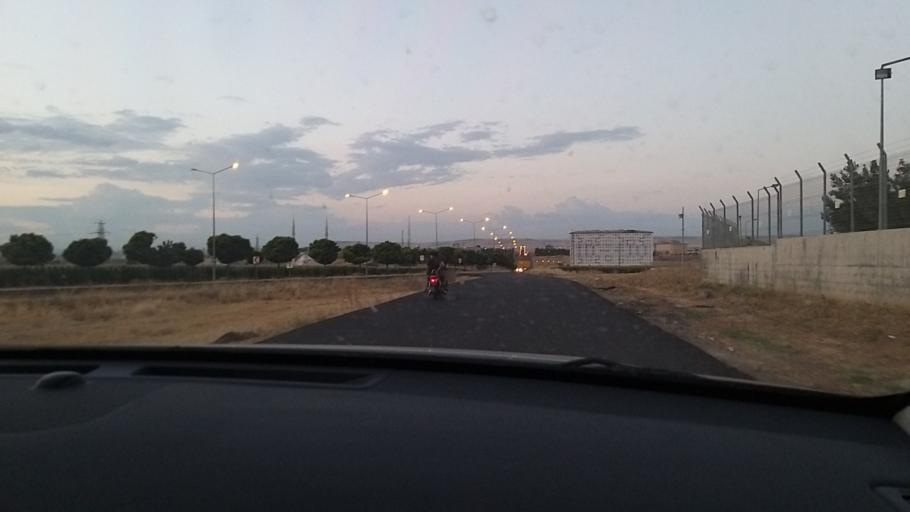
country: TR
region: Batman
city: Erkoklu
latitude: 37.8548
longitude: 41.1461
